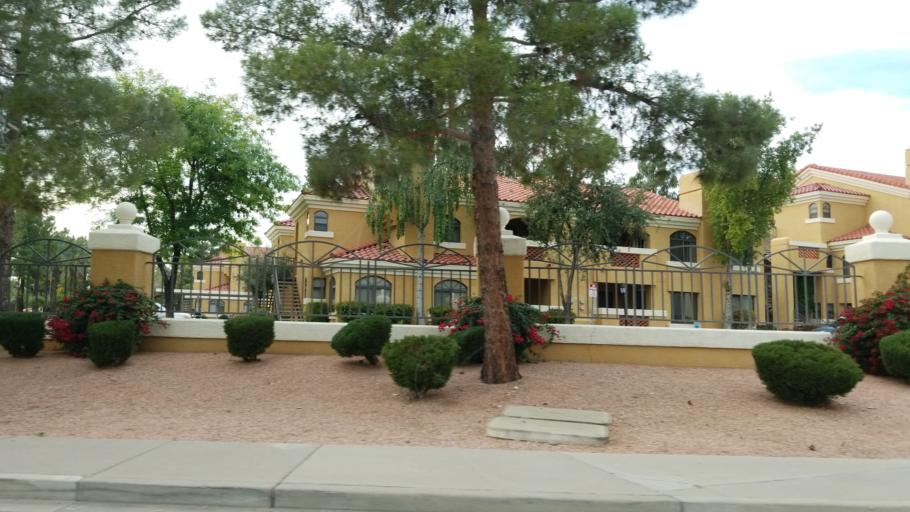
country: US
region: Arizona
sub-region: Maricopa County
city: Paradise Valley
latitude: 33.5845
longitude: -111.9303
